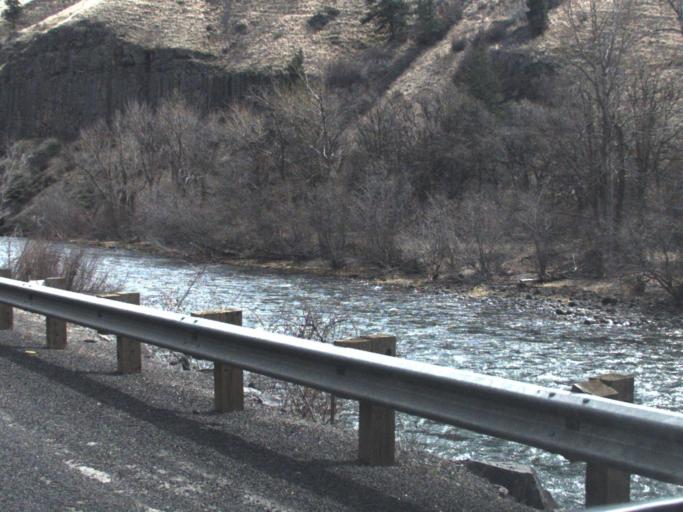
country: US
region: Washington
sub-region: Yakima County
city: Tieton
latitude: 46.7693
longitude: -120.8417
